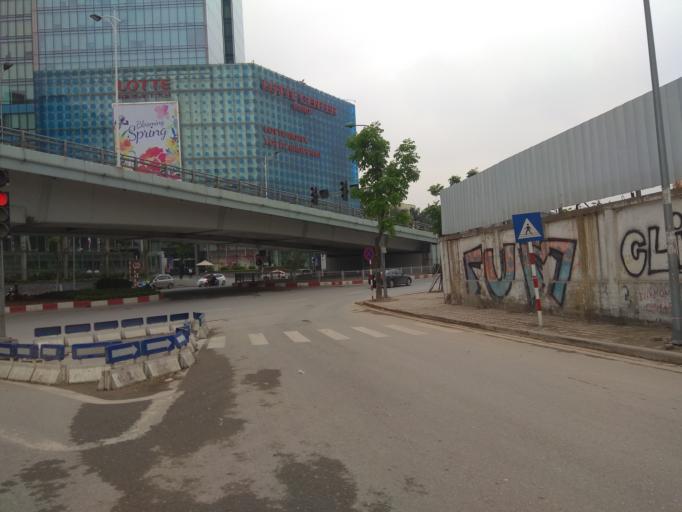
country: VN
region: Ha Noi
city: Cau Giay
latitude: 21.0314
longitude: 105.8135
